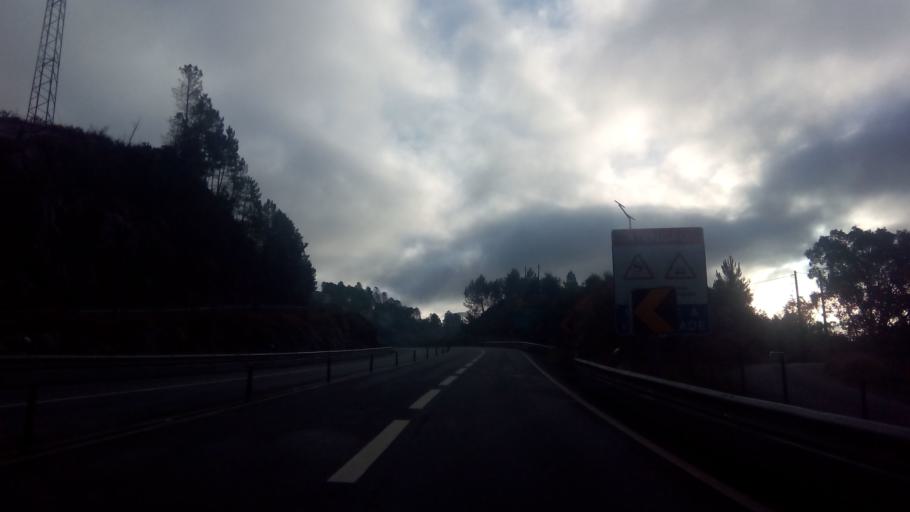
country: PT
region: Porto
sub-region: Amarante
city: Amarante
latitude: 41.2644
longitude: -8.0276
